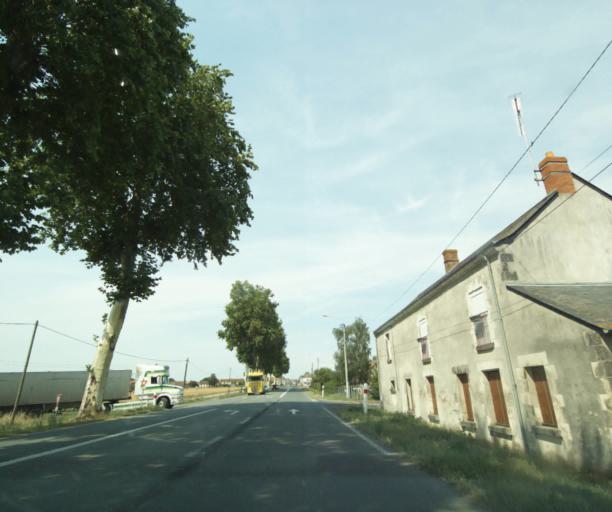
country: FR
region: Centre
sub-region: Departement d'Indre-et-Loire
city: La Celle-Saint-Avant
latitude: 47.0166
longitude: 0.6028
